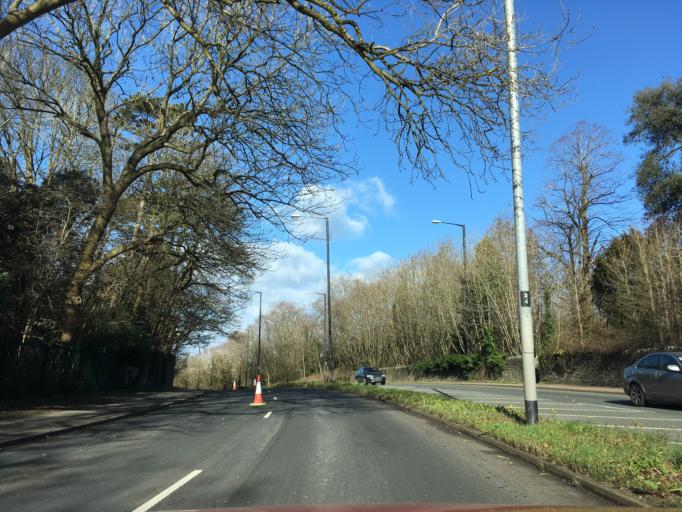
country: GB
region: England
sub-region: Bristol
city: Bristol
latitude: 51.5037
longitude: -2.6153
